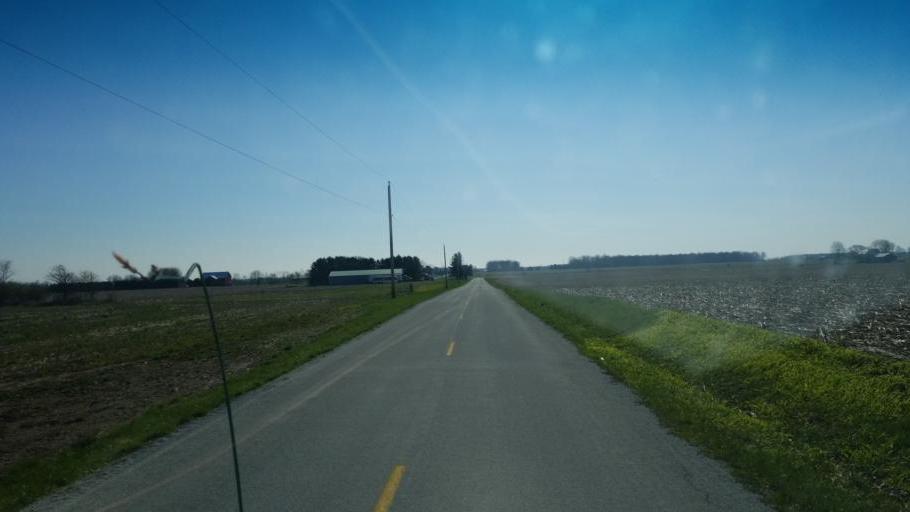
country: US
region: Ohio
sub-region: Hardin County
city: Kenton
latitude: 40.7018
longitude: -83.5436
